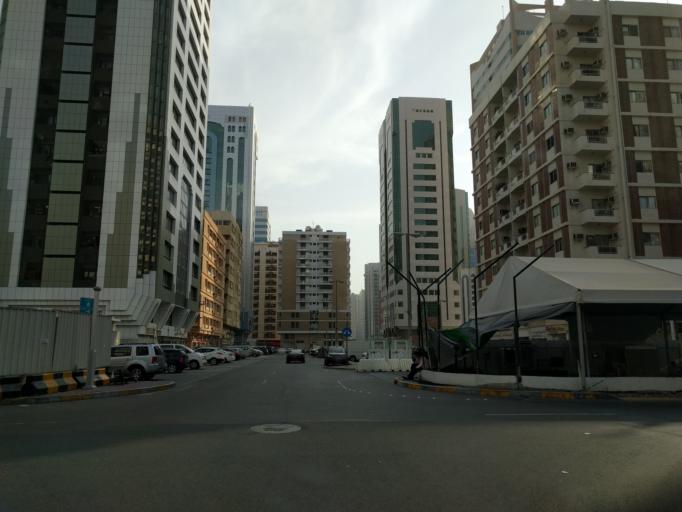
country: AE
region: Abu Dhabi
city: Abu Dhabi
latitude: 24.5010
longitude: 54.3739
